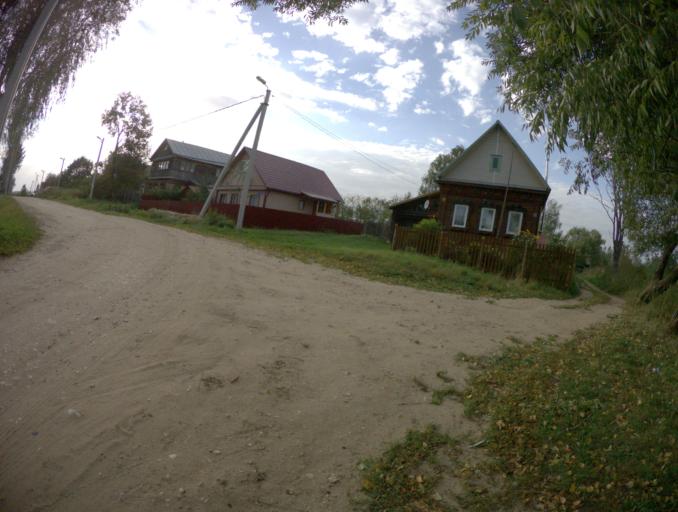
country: RU
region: Vladimir
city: Orgtrud
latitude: 56.1565
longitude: 40.6048
